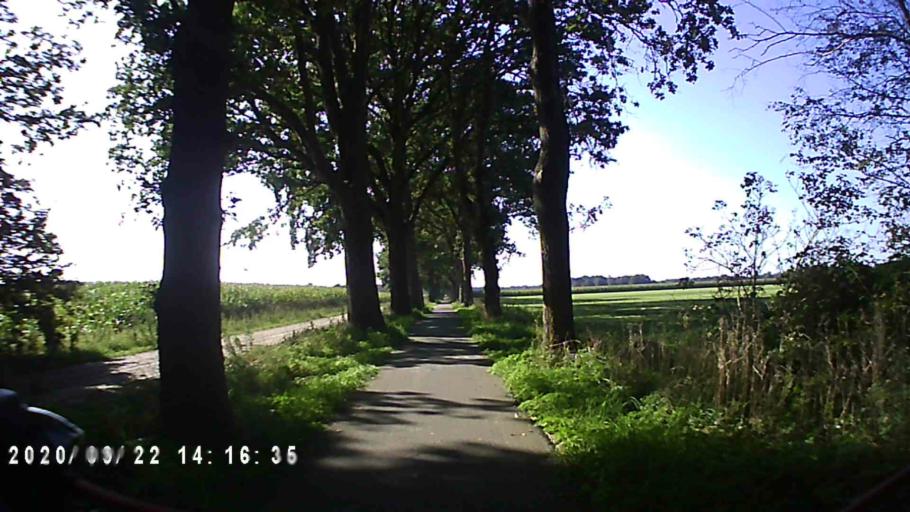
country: NL
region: Groningen
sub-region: Gemeente Leek
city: Leek
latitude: 53.0693
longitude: 6.4252
